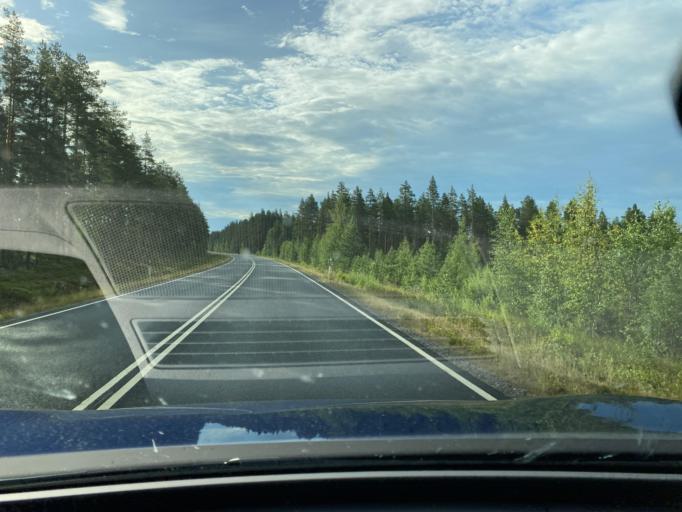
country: FI
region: Central Ostrobothnia
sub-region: Kaustinen
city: Veteli
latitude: 63.4112
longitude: 23.9581
